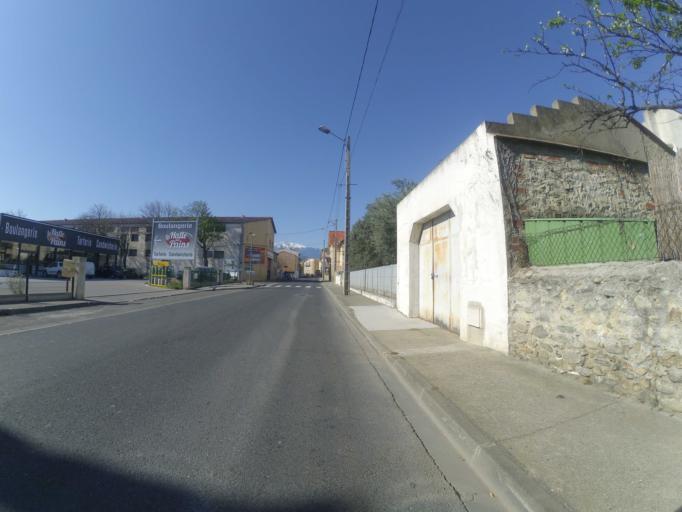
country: FR
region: Languedoc-Roussillon
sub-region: Departement des Pyrenees-Orientales
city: Ille-sur-Tet
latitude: 42.6734
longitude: 2.6241
